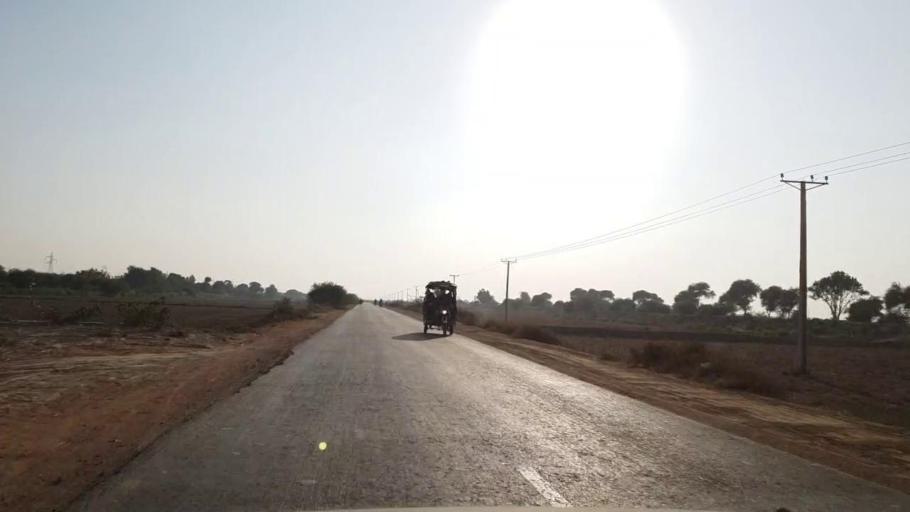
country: PK
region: Sindh
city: Mirpur Batoro
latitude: 24.7652
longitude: 68.2768
